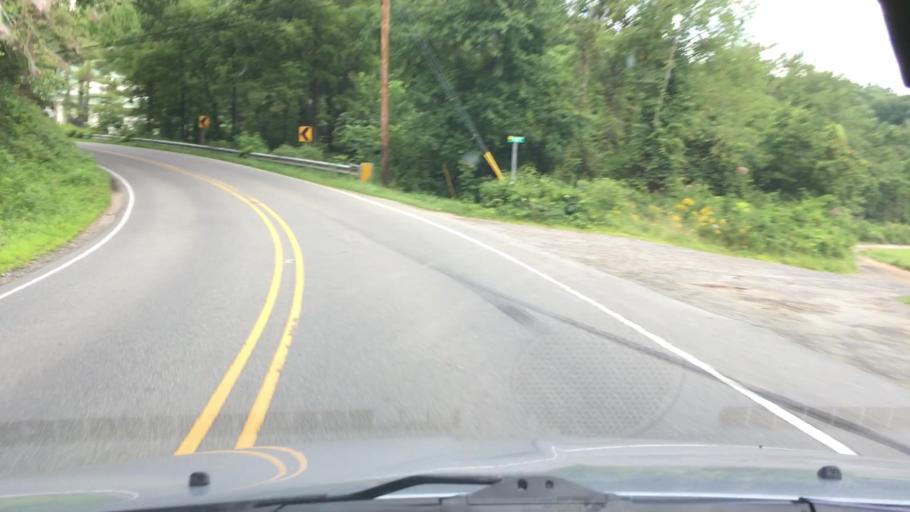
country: US
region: North Carolina
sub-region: Yancey County
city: Burnsville
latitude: 35.8438
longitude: -82.1899
